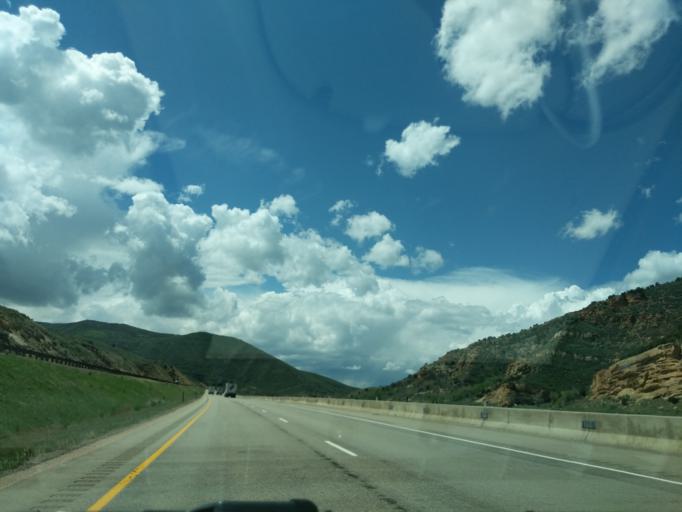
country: US
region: Utah
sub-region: Summit County
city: Coalville
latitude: 41.0569
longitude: -111.2927
